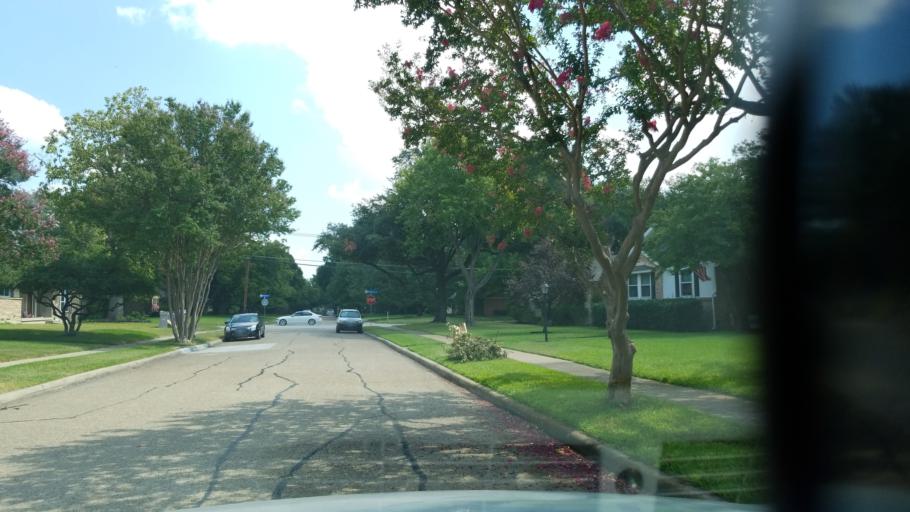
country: US
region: Texas
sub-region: Dallas County
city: Richardson
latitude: 32.9637
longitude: -96.7631
